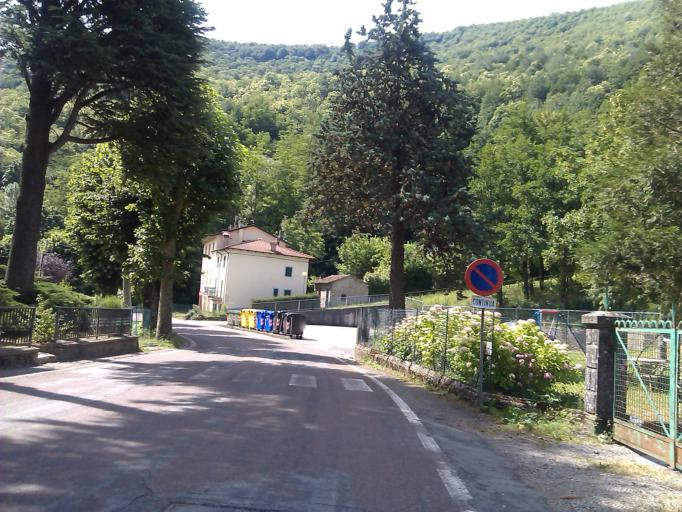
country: IT
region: Tuscany
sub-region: Provincia di Pistoia
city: Sambuca Pistoiese
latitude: 44.1180
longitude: 11.0283
